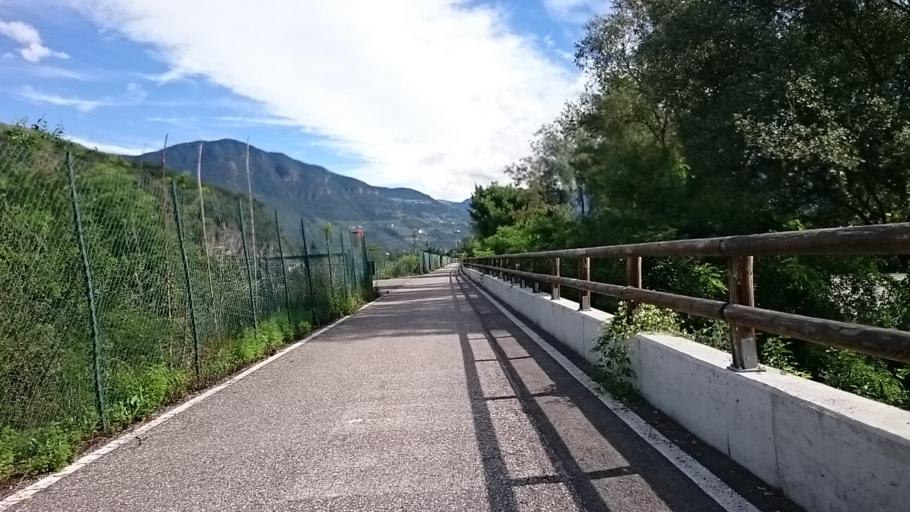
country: IT
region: Trentino-Alto Adige
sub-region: Bolzano
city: Cornaiano
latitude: 46.4685
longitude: 11.3065
